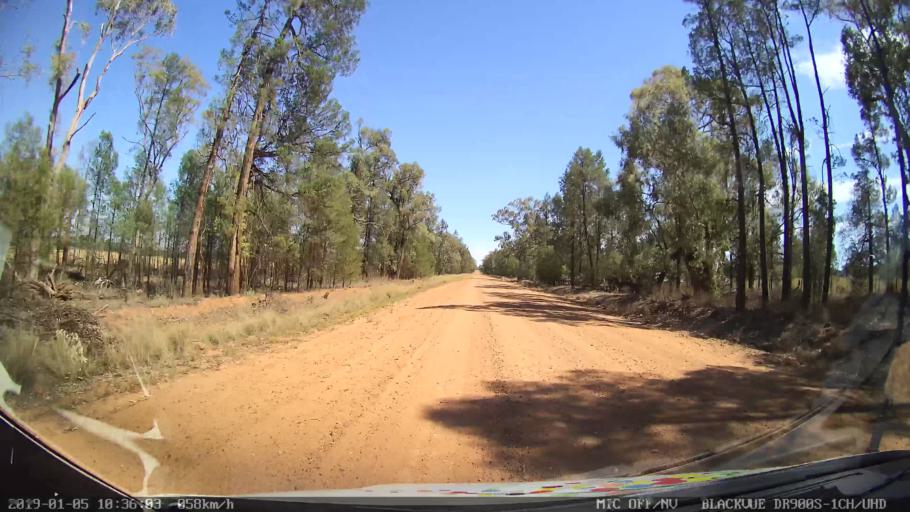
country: AU
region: New South Wales
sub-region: Gilgandra
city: Gilgandra
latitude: -31.4851
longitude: 148.9265
